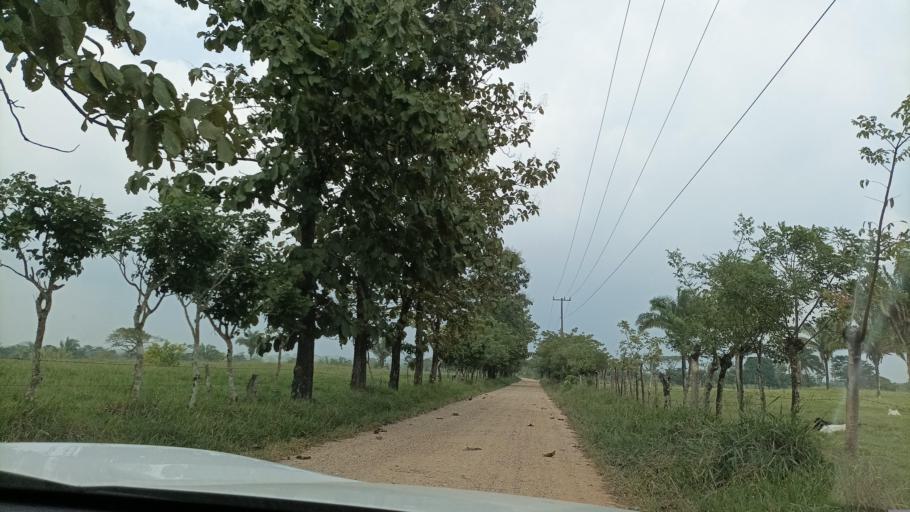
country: MX
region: Tabasco
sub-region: Huimanguillo
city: Francisco Rueda
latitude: 17.5931
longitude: -94.1983
